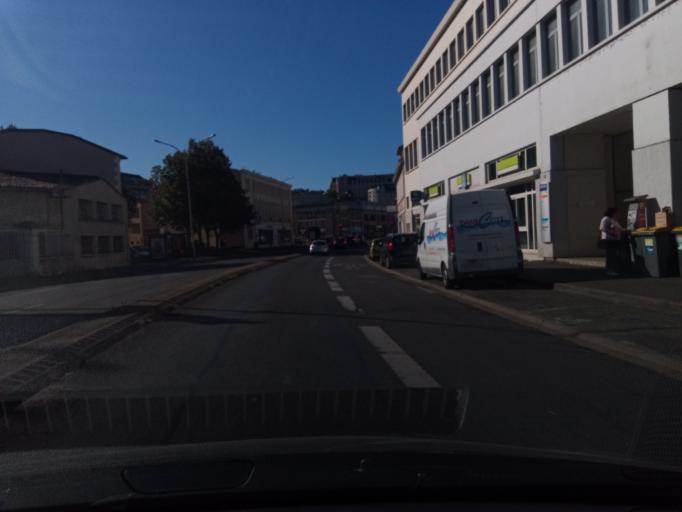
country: FR
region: Poitou-Charentes
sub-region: Departement de la Vienne
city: Poitiers
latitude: 46.5887
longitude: 0.3402
